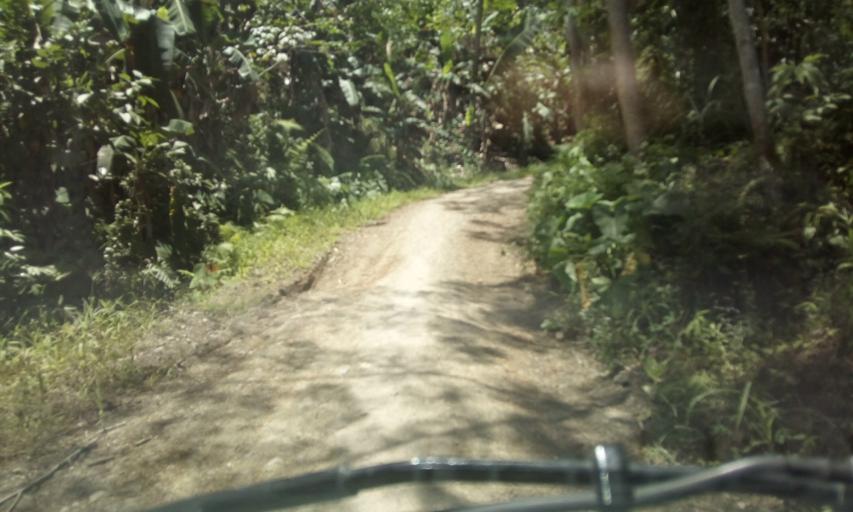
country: PH
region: Caraga
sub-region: Province of Agusan del Sur
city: Santa Josefa
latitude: 7.9543
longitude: 125.9940
